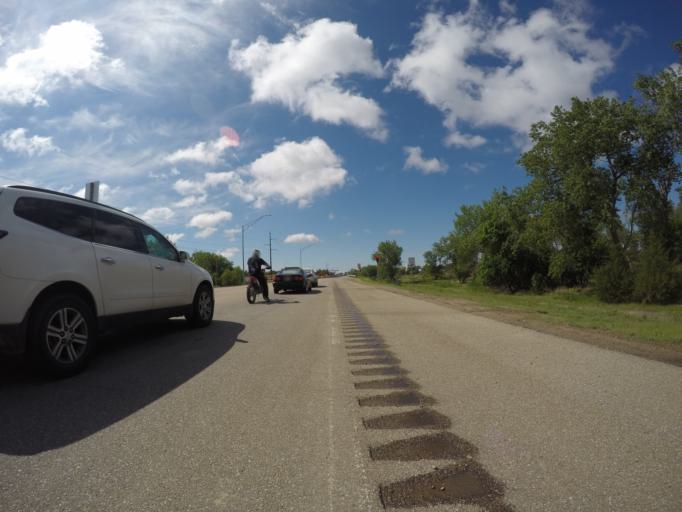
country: US
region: Nebraska
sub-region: Buffalo County
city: Kearney
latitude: 40.6603
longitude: -99.0862
